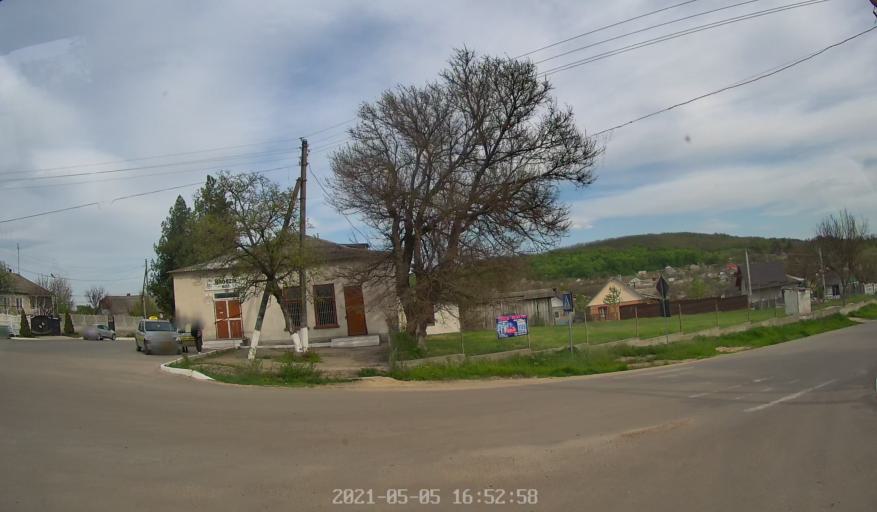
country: MD
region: Chisinau
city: Vadul lui Voda
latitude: 47.0664
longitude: 29.1323
